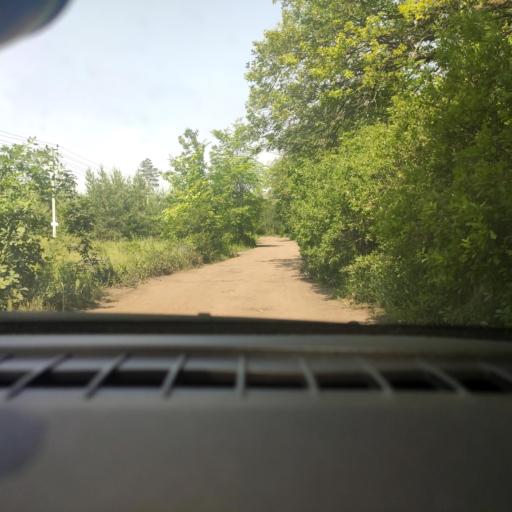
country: RU
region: Voronezj
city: Podgornoye
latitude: 51.8481
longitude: 39.2123
